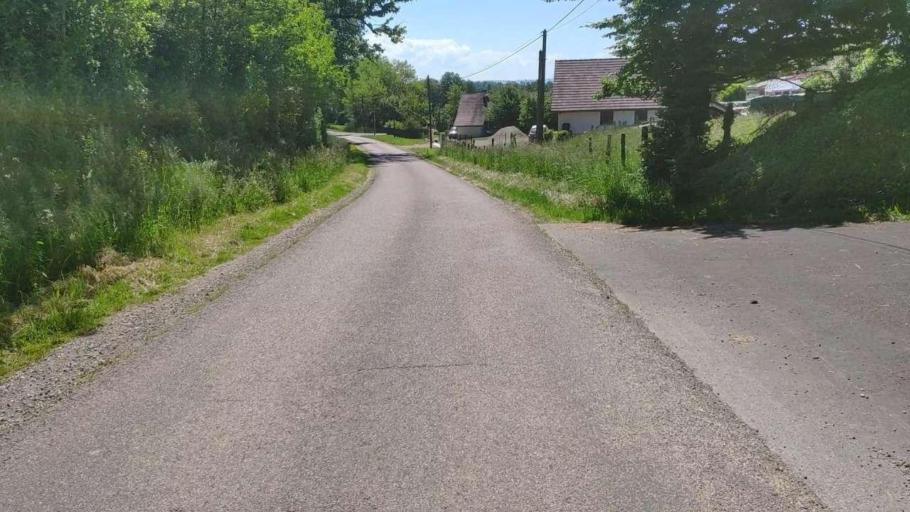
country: FR
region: Franche-Comte
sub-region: Departement du Jura
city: Bletterans
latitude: 46.7641
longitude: 5.4120
